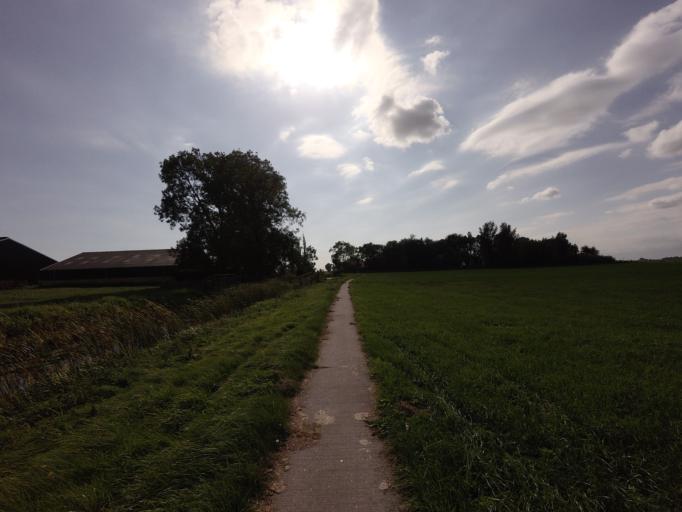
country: NL
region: Friesland
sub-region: Gemeente Littenseradiel
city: Makkum
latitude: 53.0902
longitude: 5.6355
